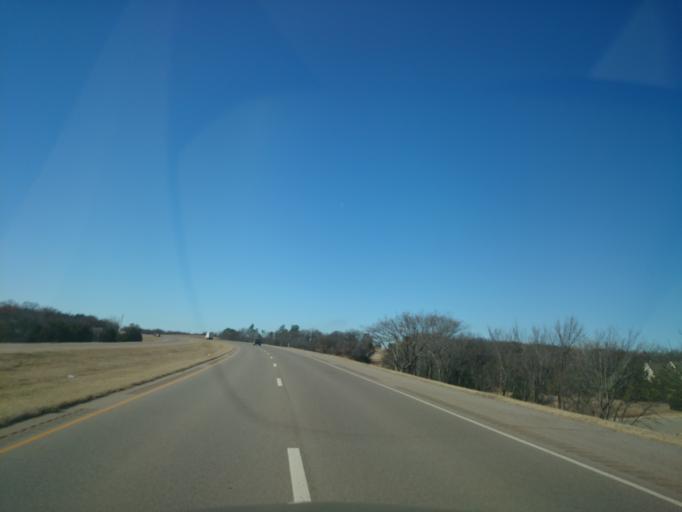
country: US
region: Oklahoma
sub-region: Payne County
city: Stillwater
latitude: 36.1161
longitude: -97.1863
